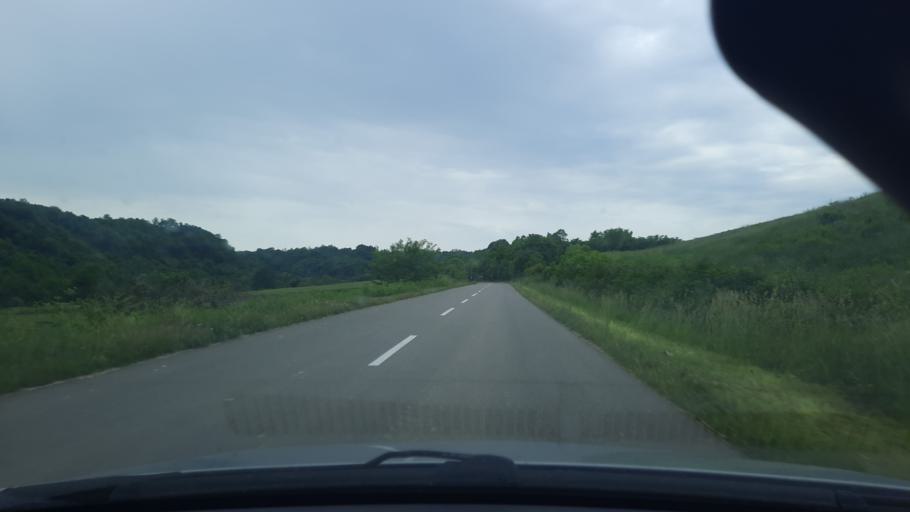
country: RS
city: Bukor
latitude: 44.5223
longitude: 19.5133
